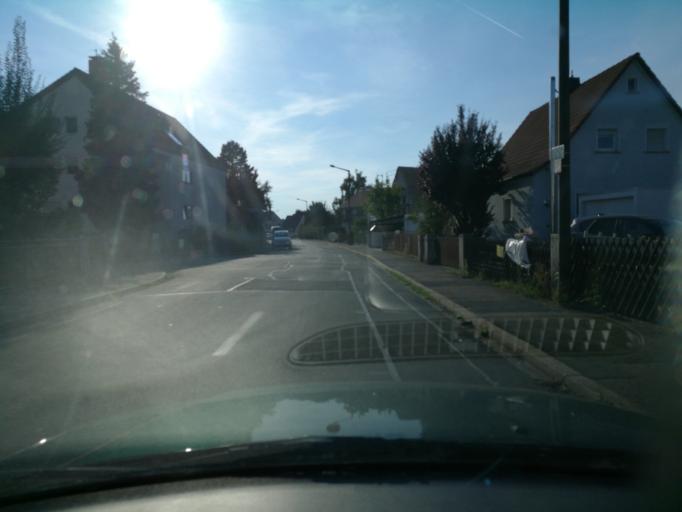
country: DE
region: Bavaria
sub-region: Regierungsbezirk Mittelfranken
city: Furth
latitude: 49.5144
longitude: 10.9810
